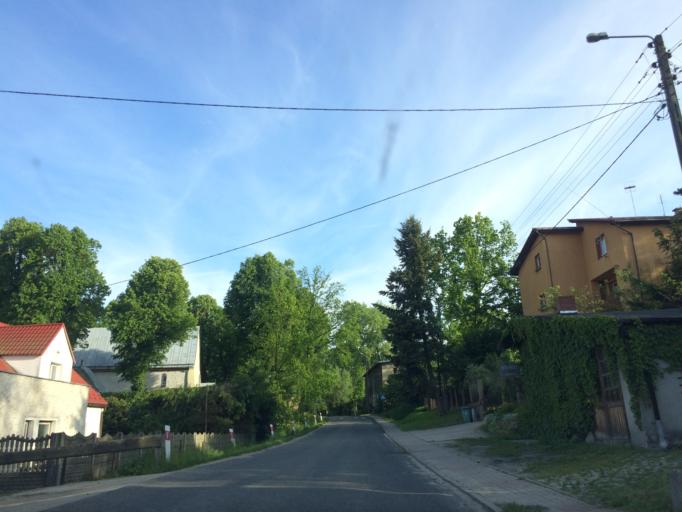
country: PL
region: Lower Silesian Voivodeship
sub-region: Powiat swidnicki
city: Swidnica
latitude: 50.7785
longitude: 16.5028
